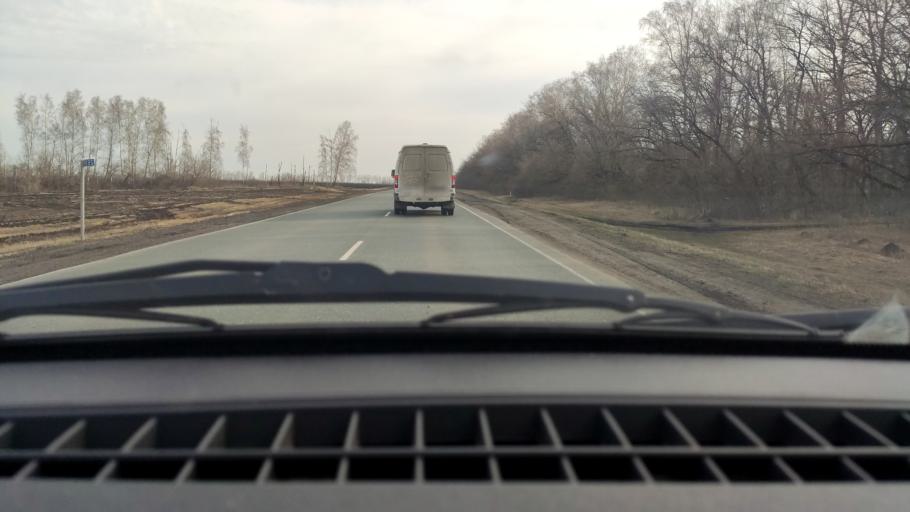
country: RU
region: Bashkortostan
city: Chishmy
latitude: 54.5391
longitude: 55.3162
